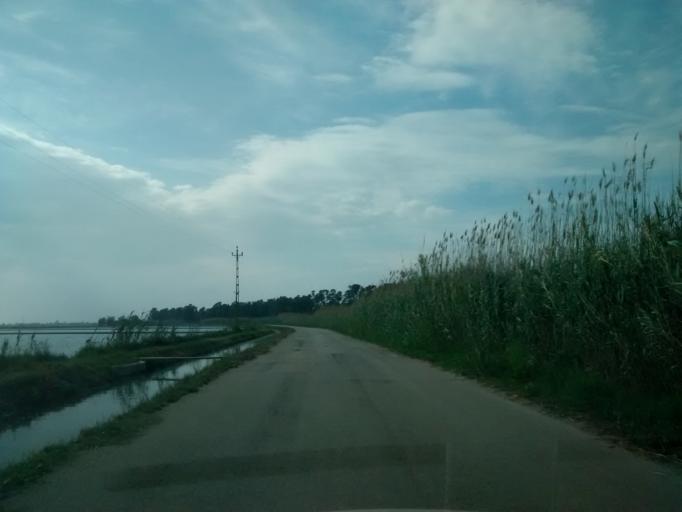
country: ES
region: Catalonia
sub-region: Provincia de Tarragona
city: Deltebre
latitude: 40.6963
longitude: 0.8362
